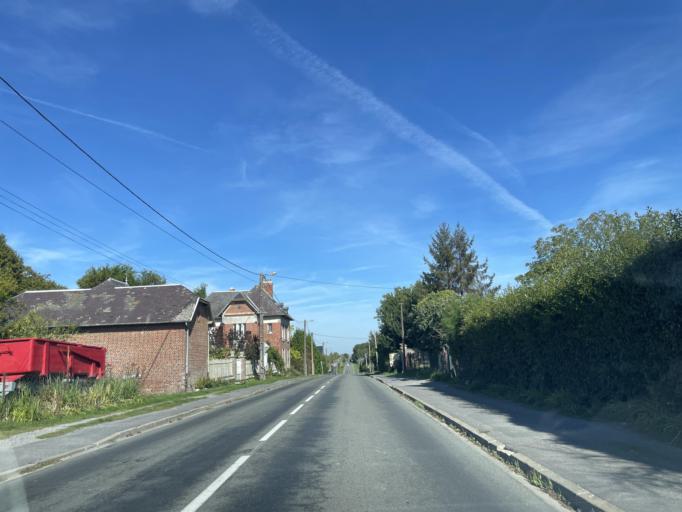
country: FR
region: Picardie
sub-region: Departement de l'Aisne
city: Guise
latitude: 49.8211
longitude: 3.6437
